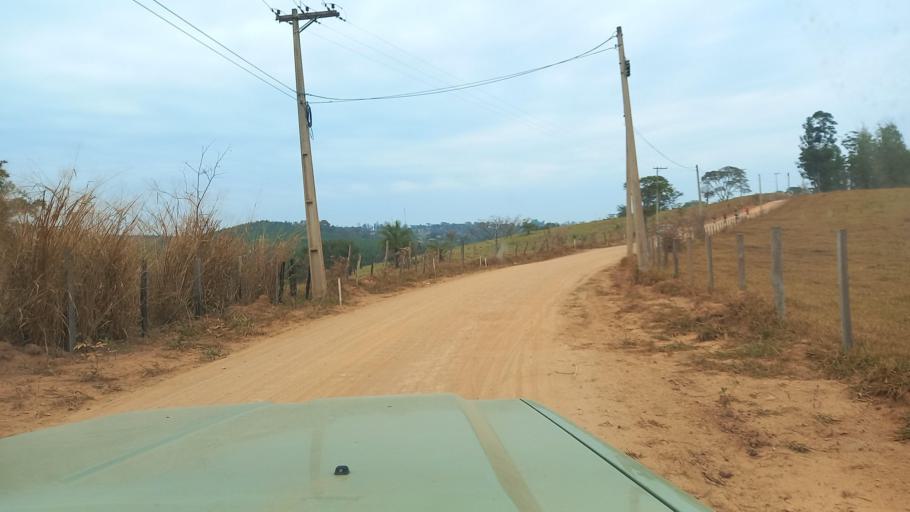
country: BR
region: Sao Paulo
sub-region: Moji-Guacu
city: Mogi-Gaucu
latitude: -22.3134
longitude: -46.8389
